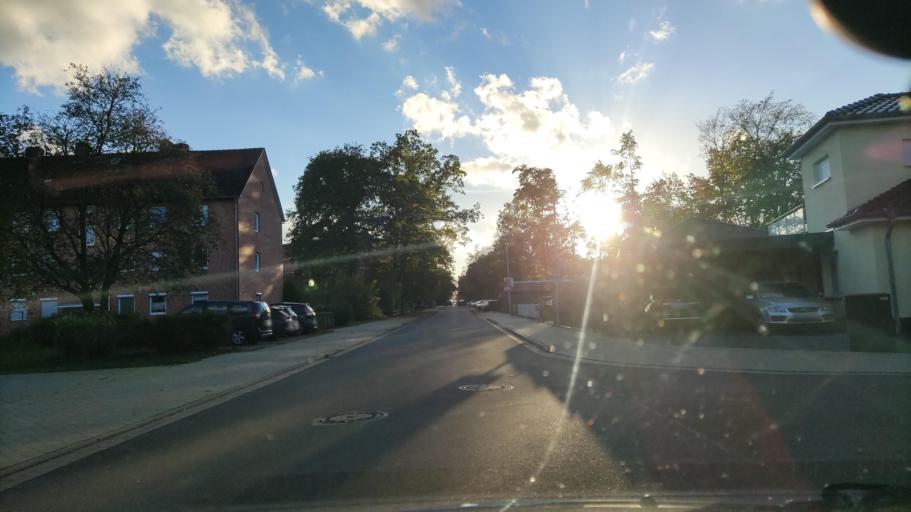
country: DE
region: Lower Saxony
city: Munster
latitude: 52.9810
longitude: 10.0837
